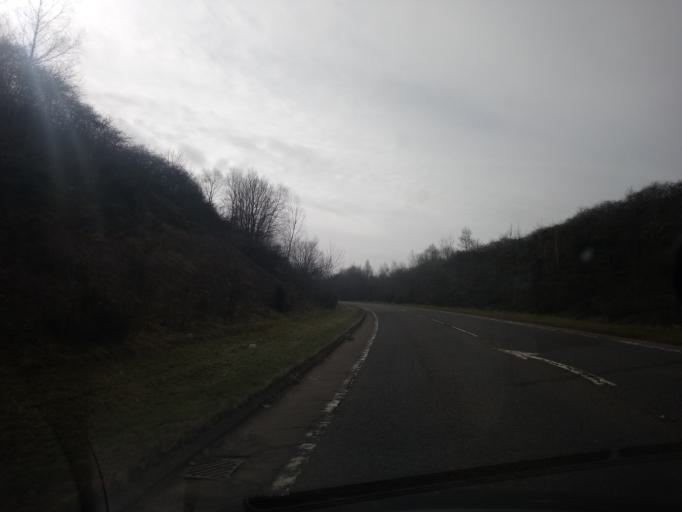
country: GB
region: England
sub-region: Telford and Wrekin
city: Ironbridge
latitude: 52.6512
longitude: -2.5057
